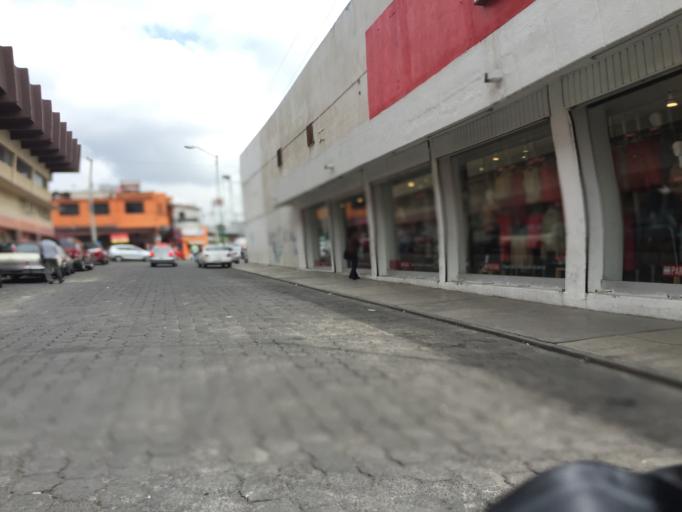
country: MX
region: Mexico
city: Cuautitlan Izcalli
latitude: 19.6524
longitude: -99.2073
